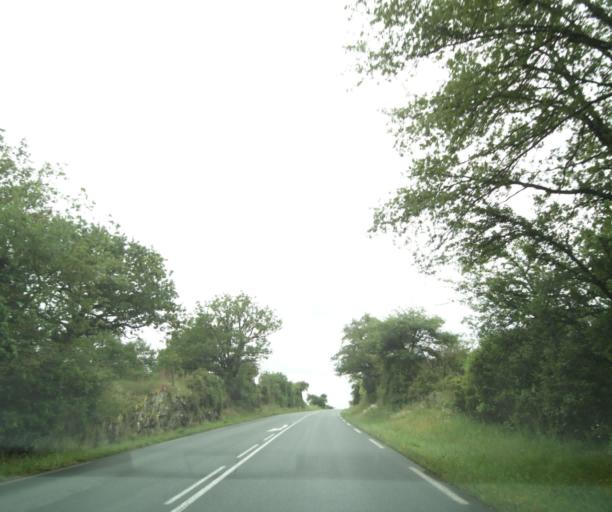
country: FR
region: Poitou-Charentes
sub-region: Departement des Deux-Sevres
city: Viennay
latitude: 46.7123
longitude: -0.2395
